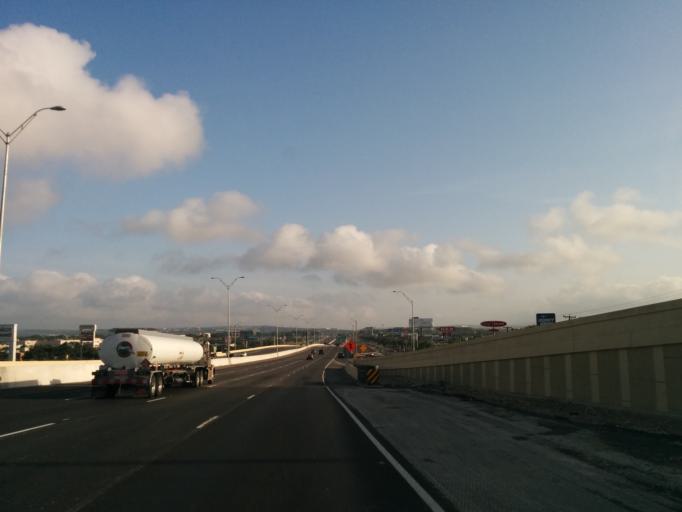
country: US
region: Texas
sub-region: Bexar County
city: Shavano Park
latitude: 29.5594
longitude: -98.5897
